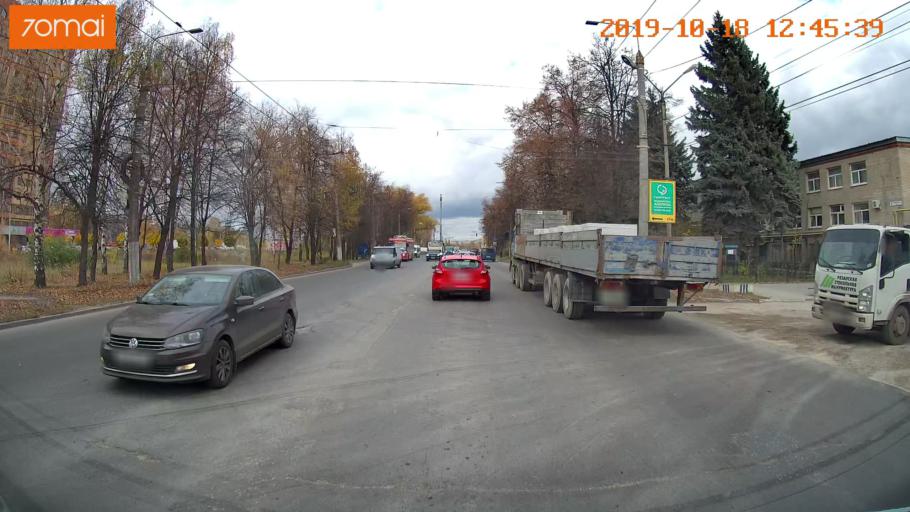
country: RU
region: Rjazan
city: Ryazan'
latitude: 54.6533
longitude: 39.6658
